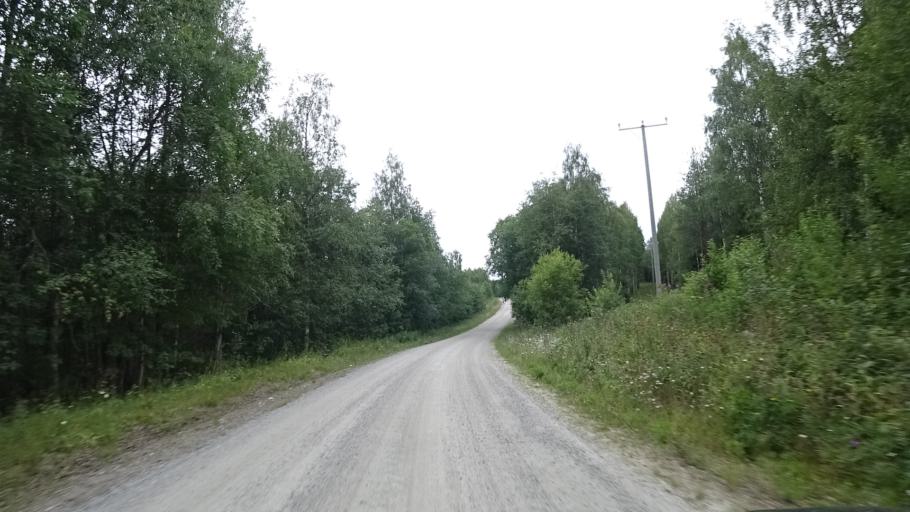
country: FI
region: North Karelia
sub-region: Joensuu
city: Eno
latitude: 63.1769
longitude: 30.5482
